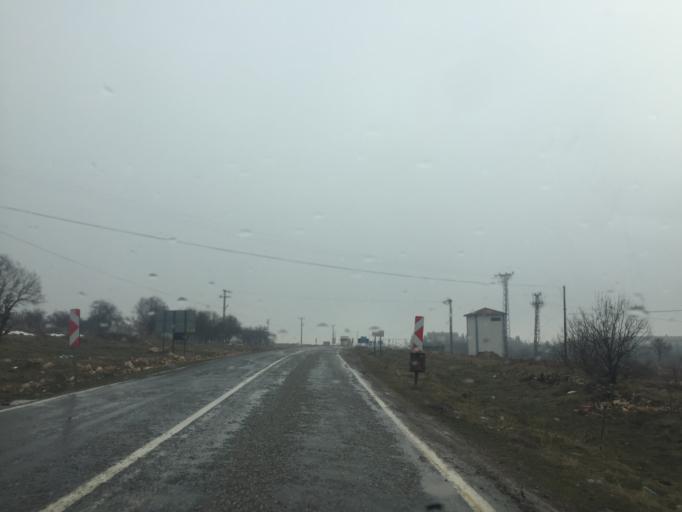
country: TR
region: Mardin
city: Omerli
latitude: 37.3972
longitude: 40.9289
